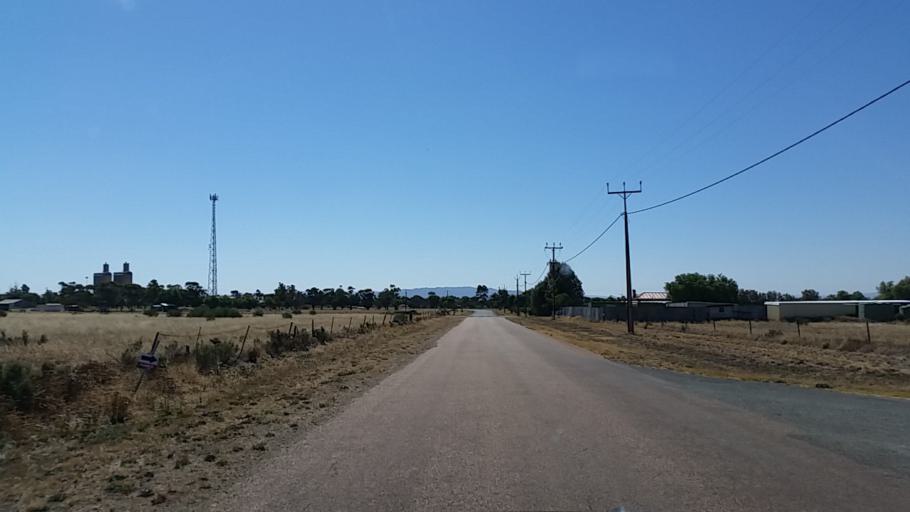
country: AU
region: South Australia
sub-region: Peterborough
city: Peterborough
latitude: -32.7366
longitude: 138.6217
